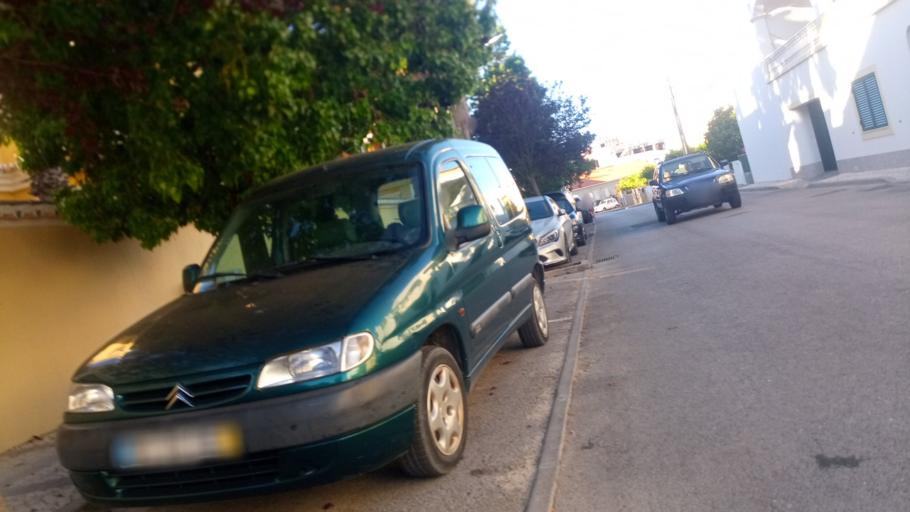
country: PT
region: Faro
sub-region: Tavira
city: Tavira
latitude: 37.1485
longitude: -7.6008
